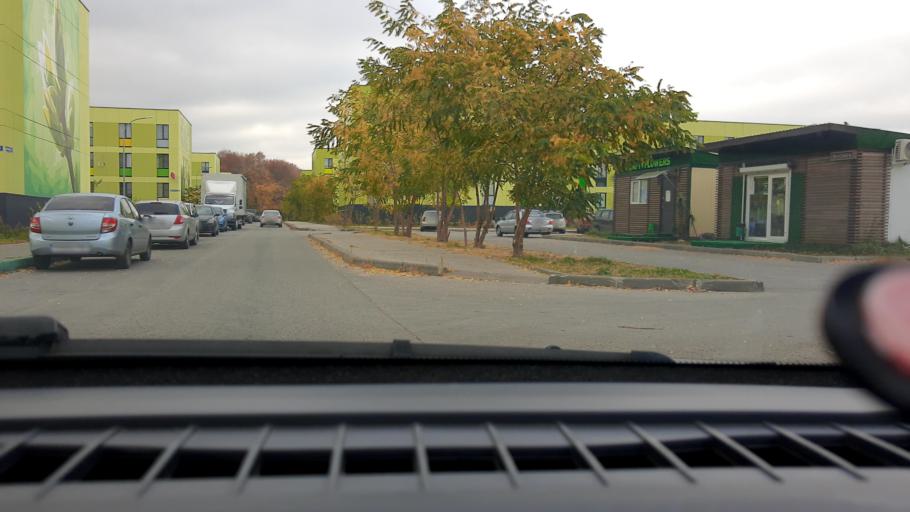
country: RU
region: Nizjnij Novgorod
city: Afonino
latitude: 56.2139
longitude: 44.0209
